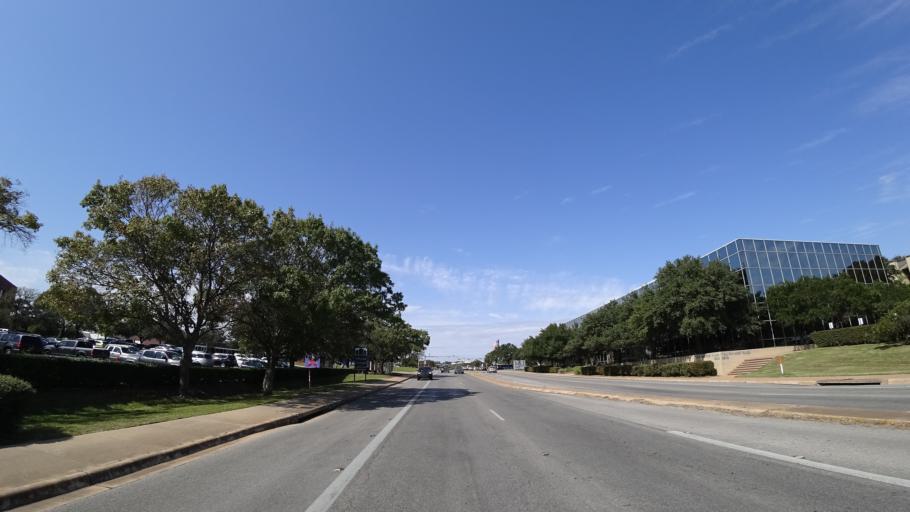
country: US
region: Texas
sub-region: Travis County
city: West Lake Hills
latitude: 30.3526
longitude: -97.7516
